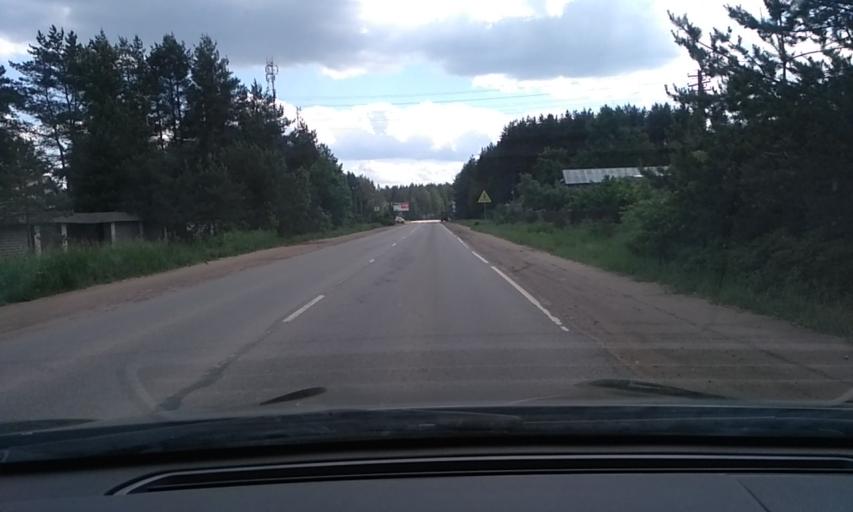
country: RU
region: Leningrad
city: Imeni Sverdlova
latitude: 59.8618
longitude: 30.6713
